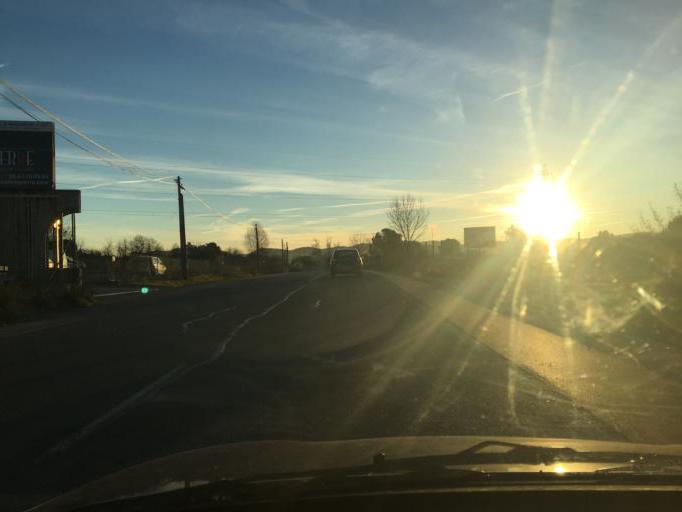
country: FR
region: Provence-Alpes-Cote d'Azur
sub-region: Departement du Var
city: Les Arcs
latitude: 43.4504
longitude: 6.4634
